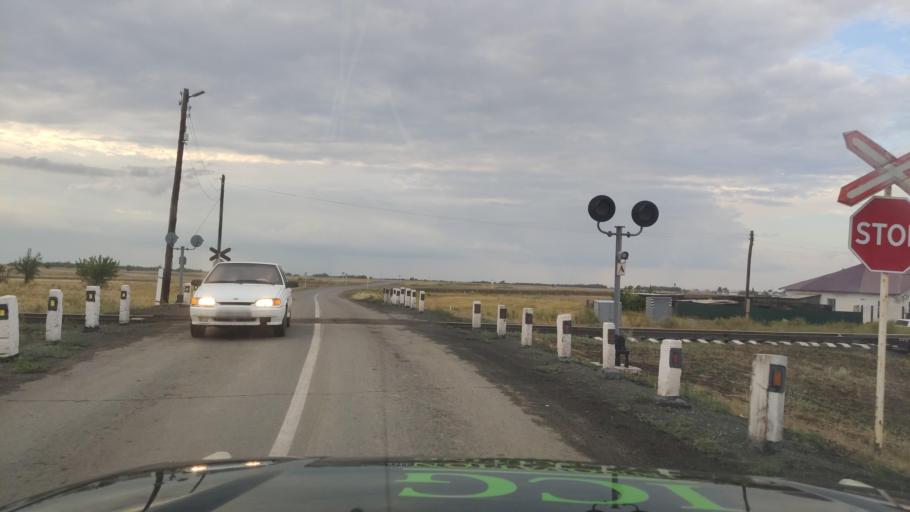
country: KZ
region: Pavlodar
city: Pavlodar
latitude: 52.3455
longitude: 77.2536
